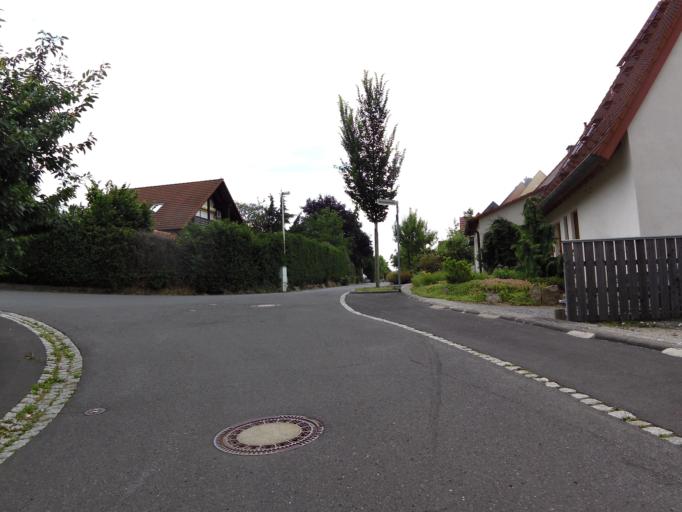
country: DE
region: Bavaria
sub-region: Regierungsbezirk Unterfranken
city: Eibelstadt
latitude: 49.7216
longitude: 9.9712
